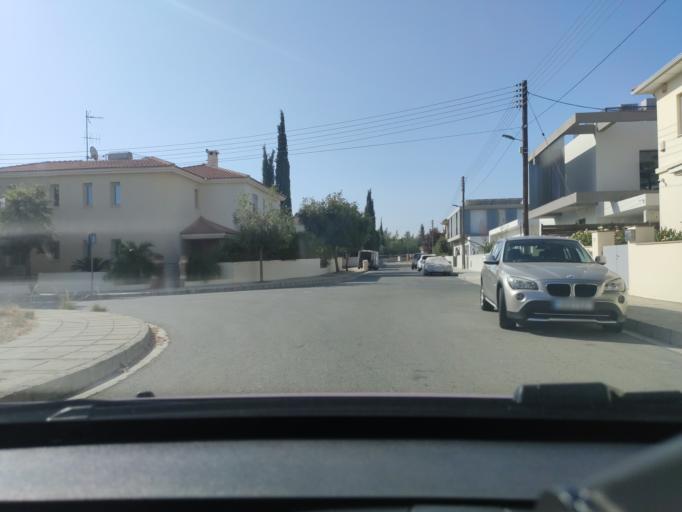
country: CY
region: Lefkosia
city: Tseri
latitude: 35.1066
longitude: 33.3530
